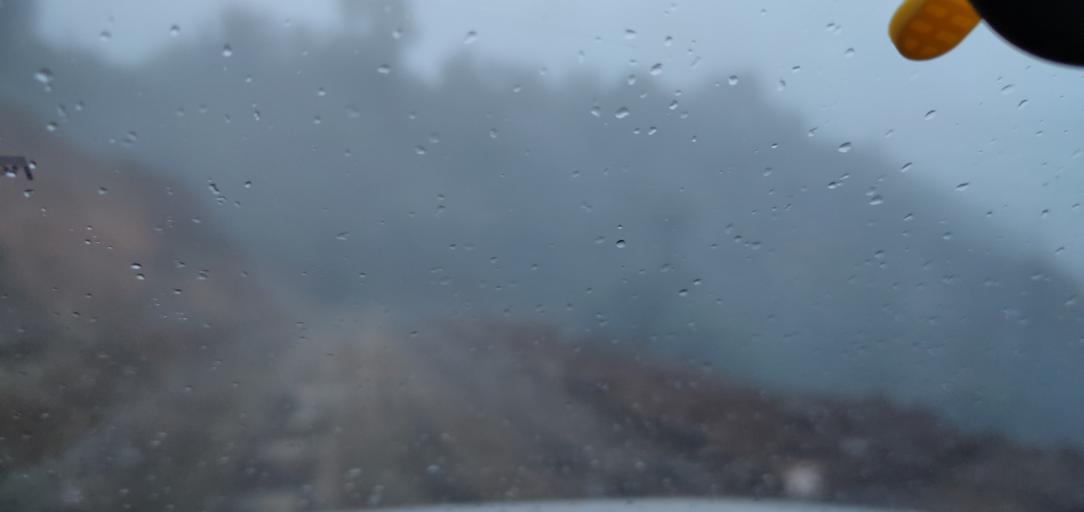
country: LA
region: Phongsali
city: Phongsali
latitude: 21.4198
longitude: 102.2510
